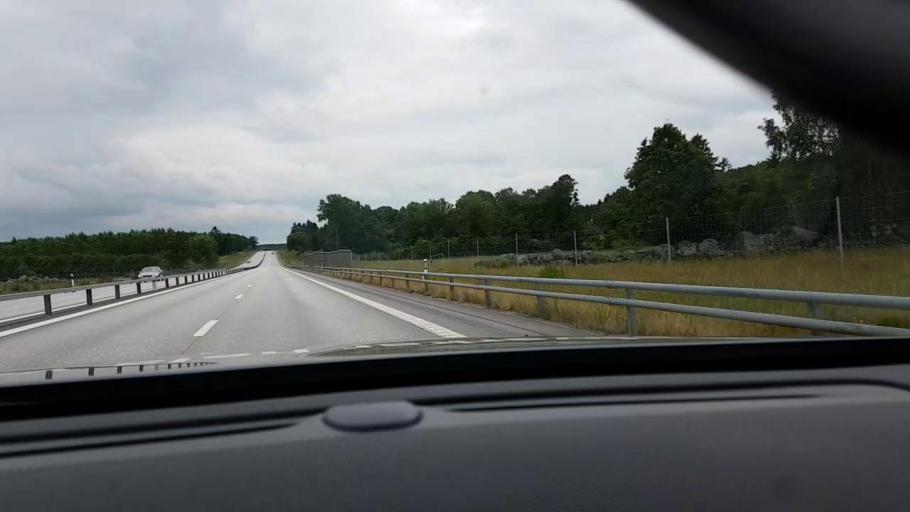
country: SE
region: Skane
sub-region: Horby Kommun
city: Hoerby
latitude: 55.8863
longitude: 13.7169
